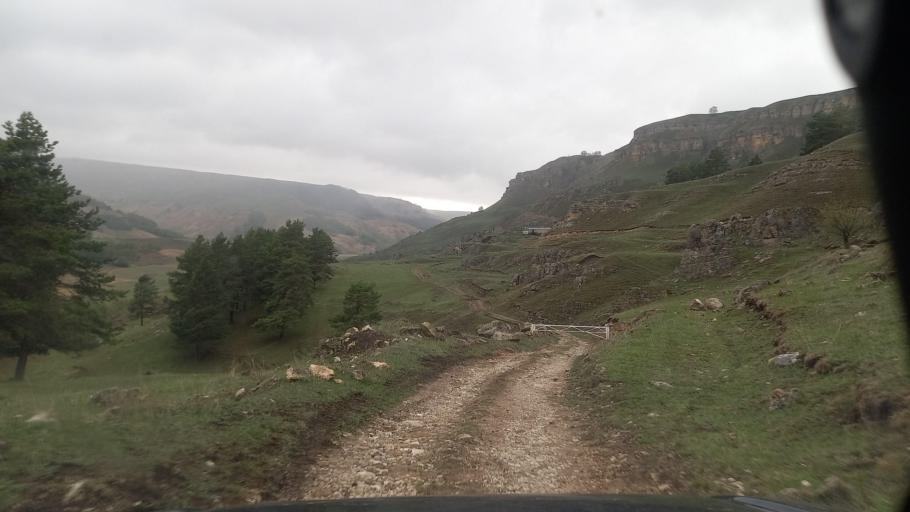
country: RU
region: Stavropol'skiy
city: Nezhinskiy
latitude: 43.8469
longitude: 42.6321
